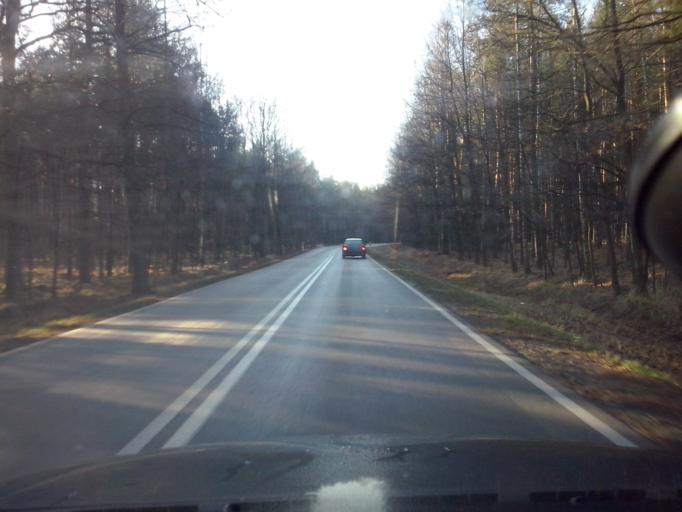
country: PL
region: Subcarpathian Voivodeship
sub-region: Powiat nizanski
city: Rudnik nad Sanem
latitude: 50.3902
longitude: 22.2716
